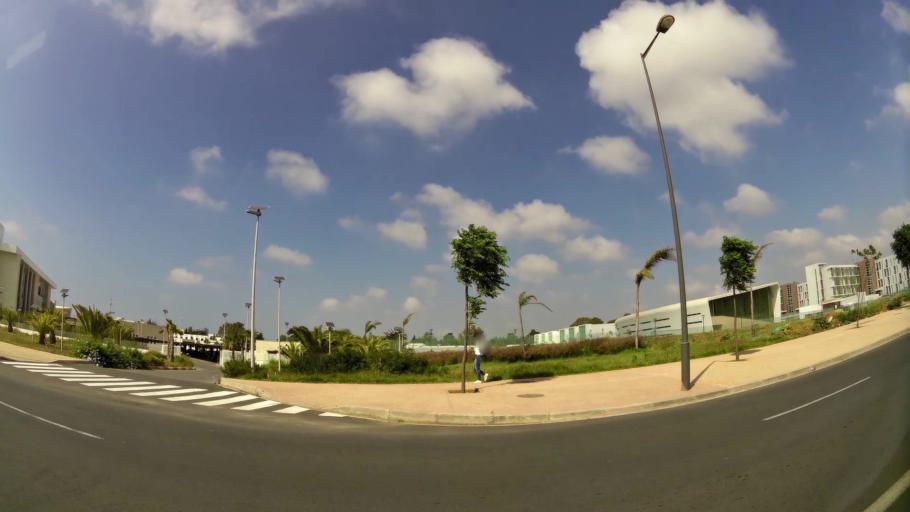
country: MA
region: Rabat-Sale-Zemmour-Zaer
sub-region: Rabat
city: Rabat
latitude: 33.9724
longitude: -6.8699
